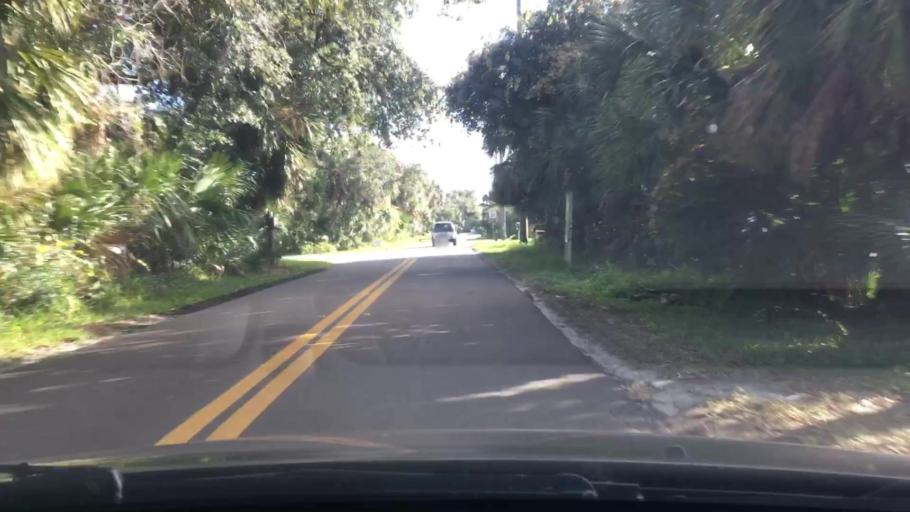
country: US
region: Florida
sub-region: Volusia County
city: Ormond-by-the-Sea
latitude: 29.3851
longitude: -81.0882
